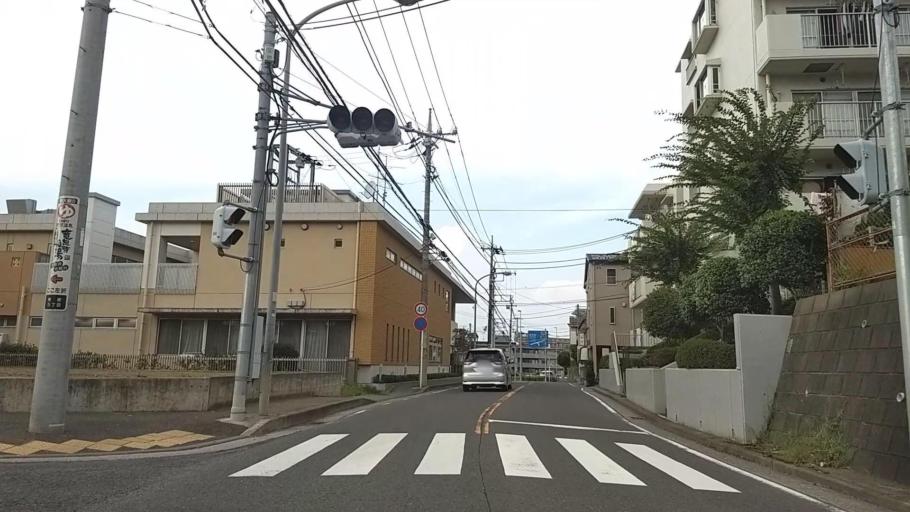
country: JP
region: Kanagawa
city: Yokohama
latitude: 35.5038
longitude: 139.5635
